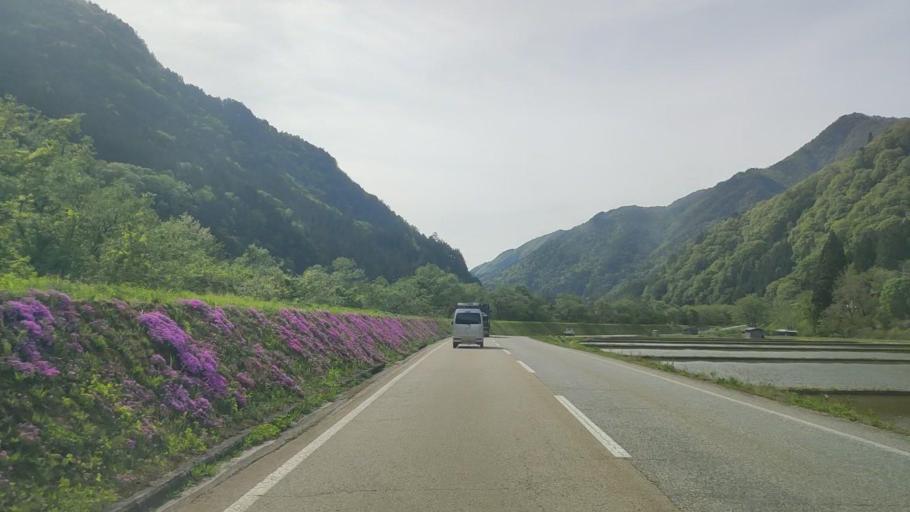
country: JP
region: Gifu
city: Takayama
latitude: 36.2607
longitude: 137.4337
